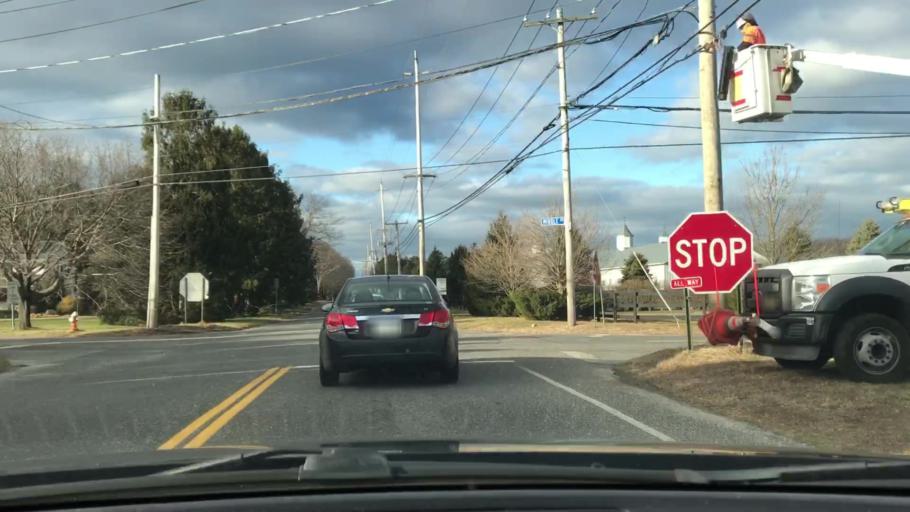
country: US
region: New York
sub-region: Suffolk County
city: Baiting Hollow
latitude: 40.9342
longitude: -72.7047
